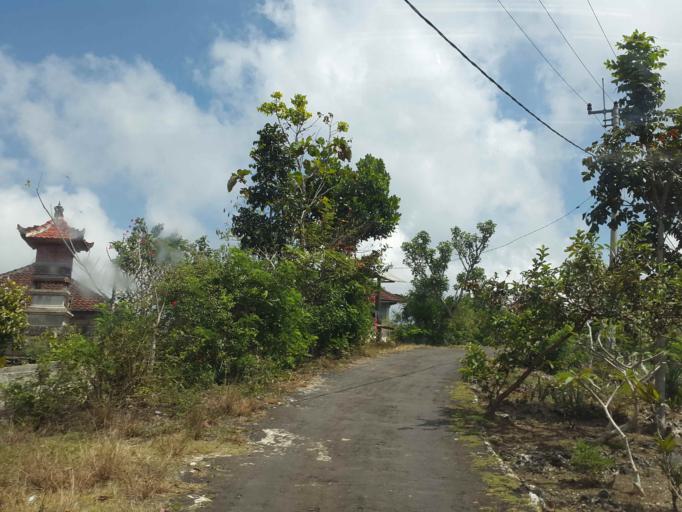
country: ID
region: Bali
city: Klumbu
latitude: -8.7334
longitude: 115.5288
